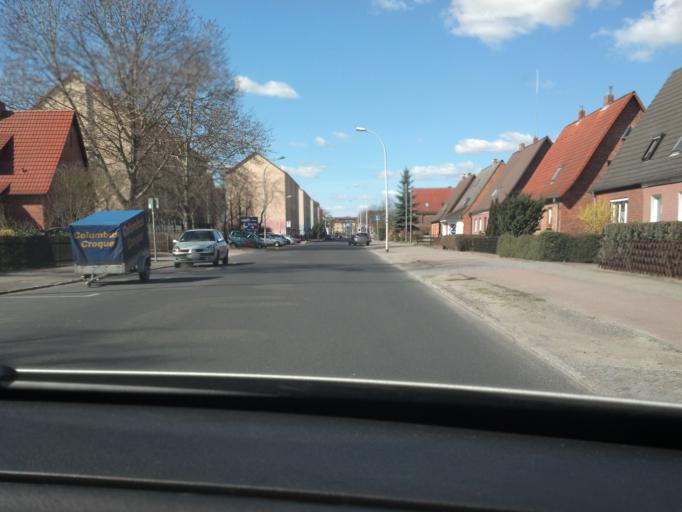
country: DE
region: Mecklenburg-Vorpommern
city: Neubrandenburg
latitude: 53.5627
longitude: 13.2784
